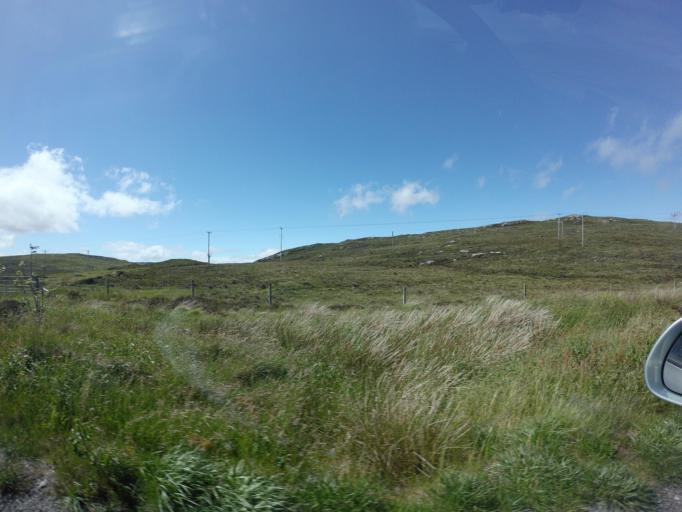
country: GB
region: Scotland
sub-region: Eilean Siar
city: Stornoway
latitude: 58.1269
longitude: -6.5070
